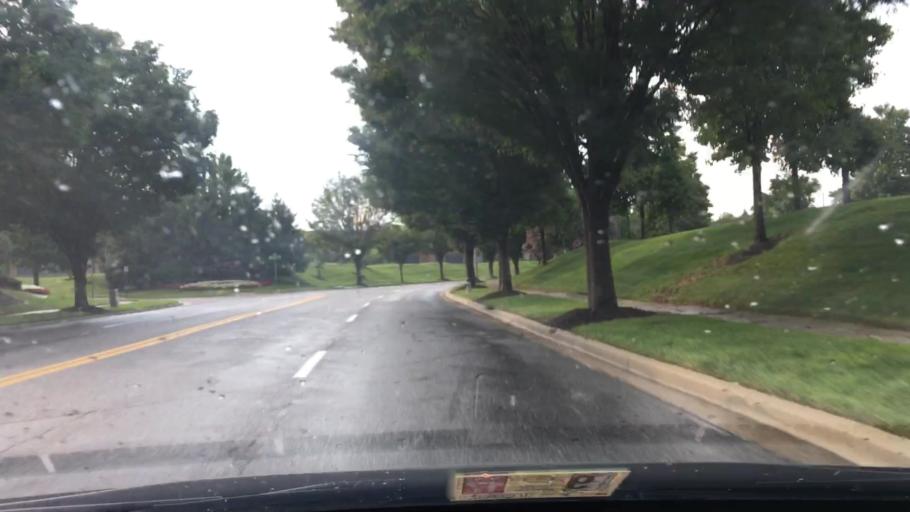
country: US
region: Maryland
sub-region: Prince George's County
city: Beltsville
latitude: 39.0615
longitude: -76.8882
